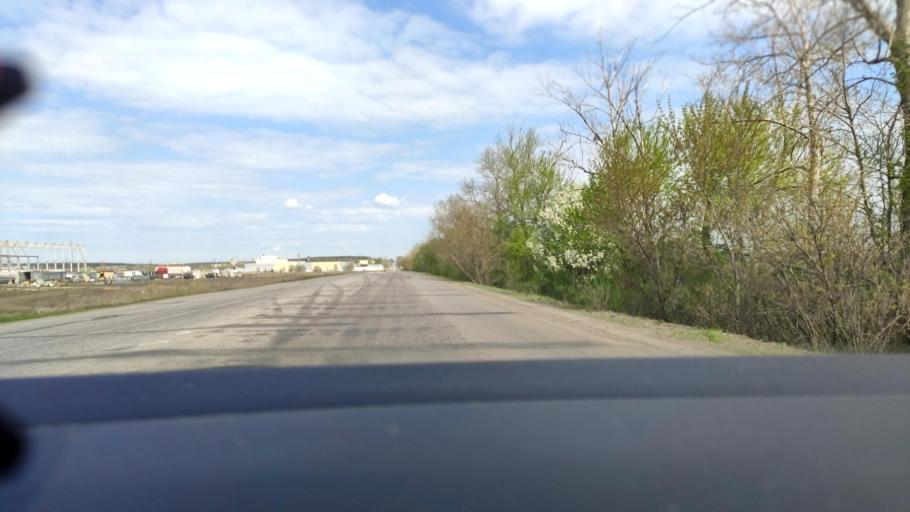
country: RU
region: Voronezj
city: Maslovka
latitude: 51.5411
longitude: 39.2865
